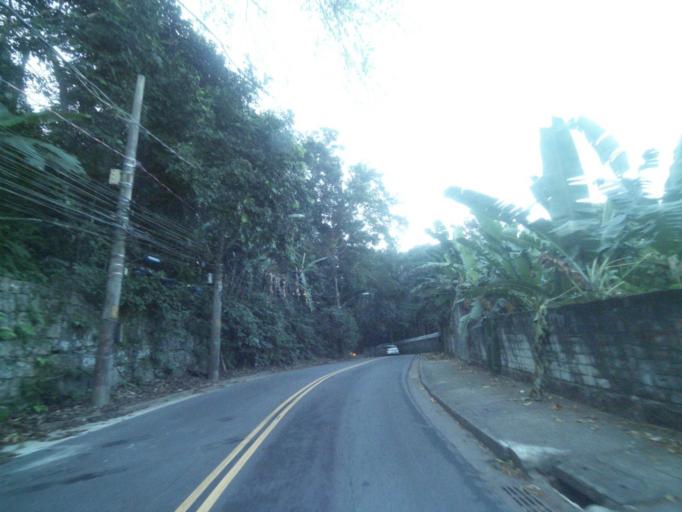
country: BR
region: Rio de Janeiro
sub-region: Rio De Janeiro
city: Rio de Janeiro
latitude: -23.0047
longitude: -43.2814
